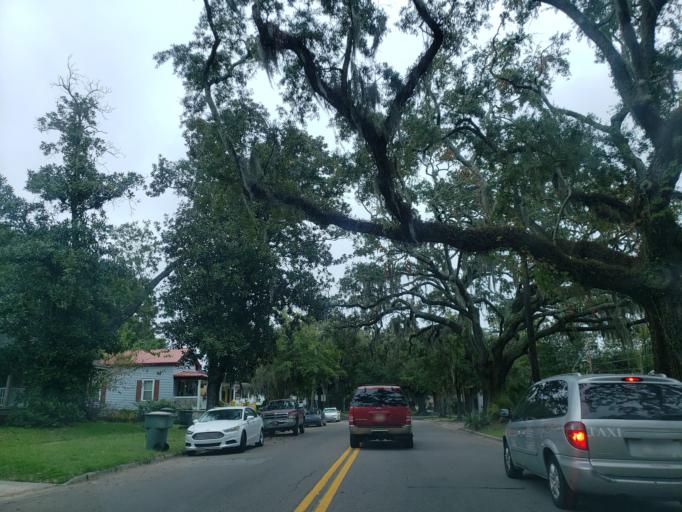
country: US
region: Georgia
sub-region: Chatham County
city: Savannah
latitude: 32.0533
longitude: -81.0857
